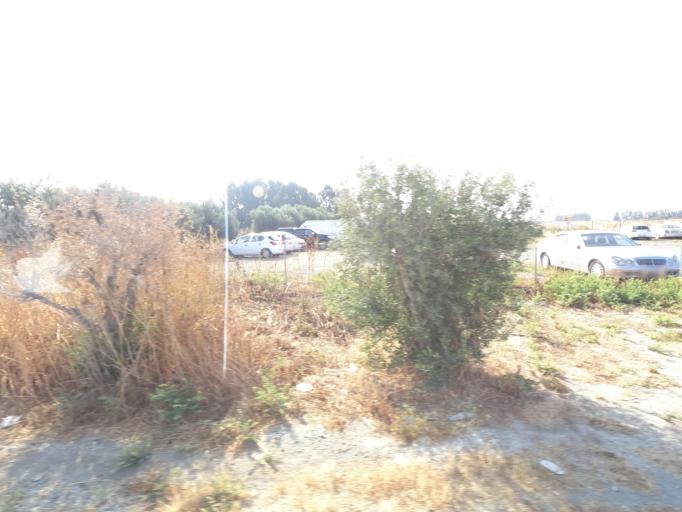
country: CY
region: Larnaka
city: Meneou
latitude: 34.8699
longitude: 33.6025
